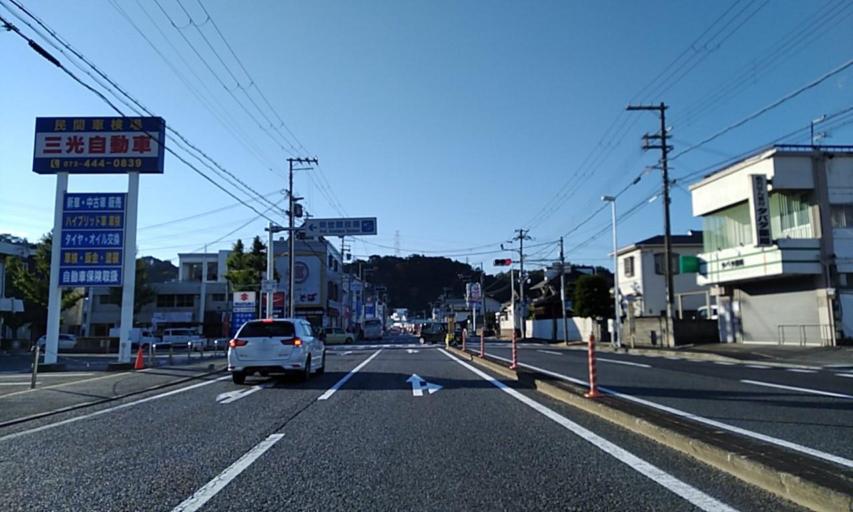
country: JP
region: Wakayama
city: Kainan
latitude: 34.1669
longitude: 135.1873
